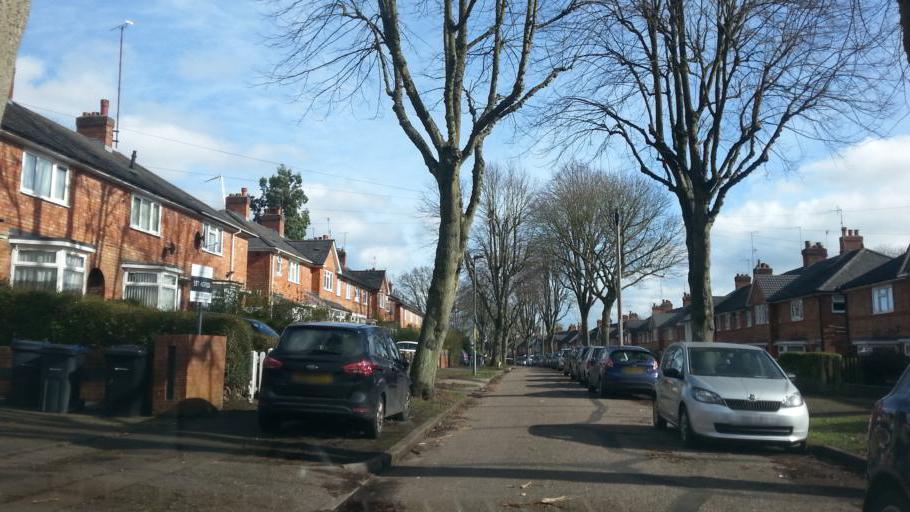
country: GB
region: England
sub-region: City and Borough of Birmingham
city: Bartley Green
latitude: 52.4472
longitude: -1.9520
